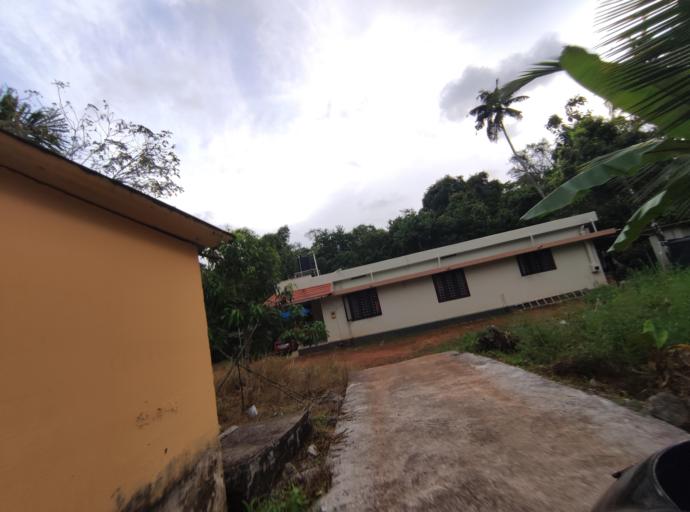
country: IN
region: Kerala
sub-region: Alappuzha
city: Shertallai
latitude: 9.6305
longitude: 76.4256
